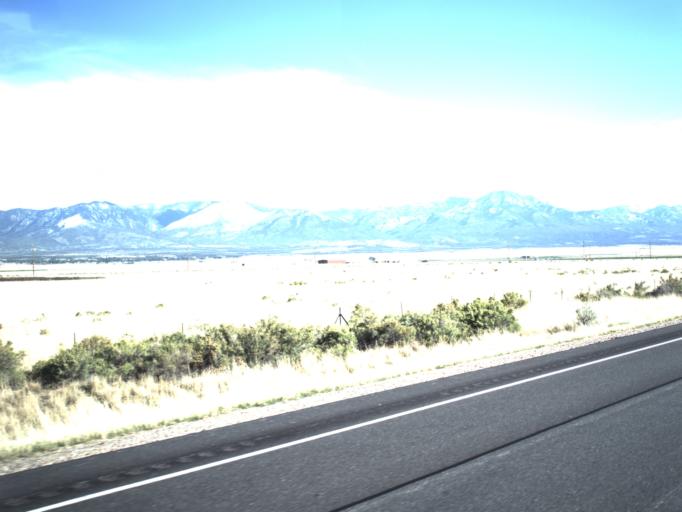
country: US
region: Utah
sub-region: Millard County
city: Fillmore
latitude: 39.1288
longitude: -112.3599
